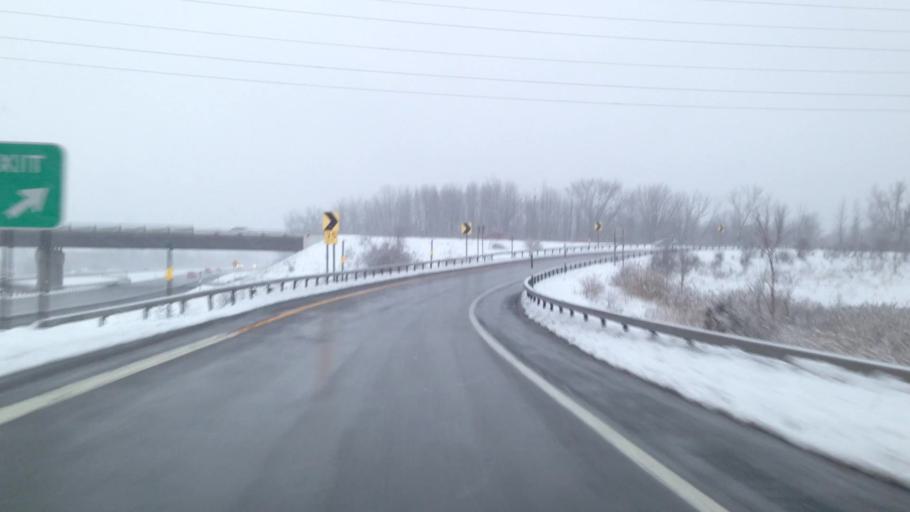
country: US
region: New York
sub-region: Onondaga County
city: East Syracuse
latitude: 43.0971
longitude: -76.0533
